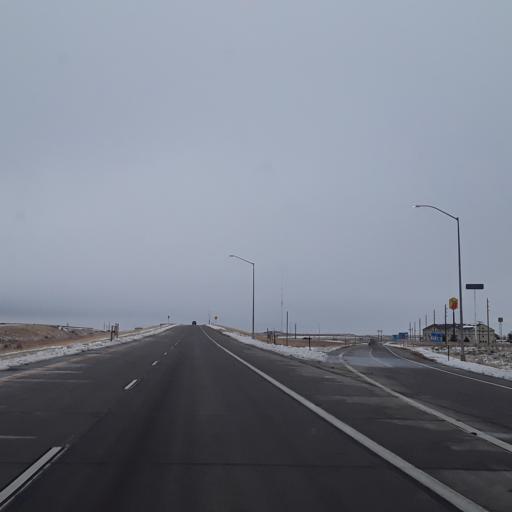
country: US
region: Colorado
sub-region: Logan County
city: Sterling
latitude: 40.6171
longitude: -103.1745
